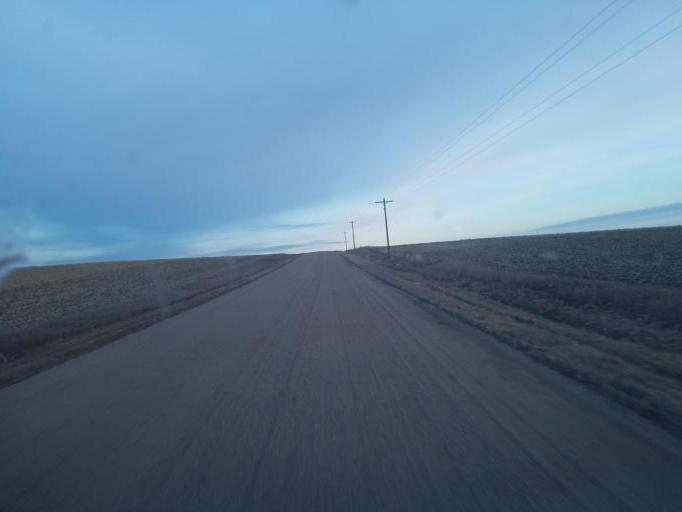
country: US
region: Nebraska
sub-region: Knox County
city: Center
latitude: 42.6263
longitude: -97.7671
